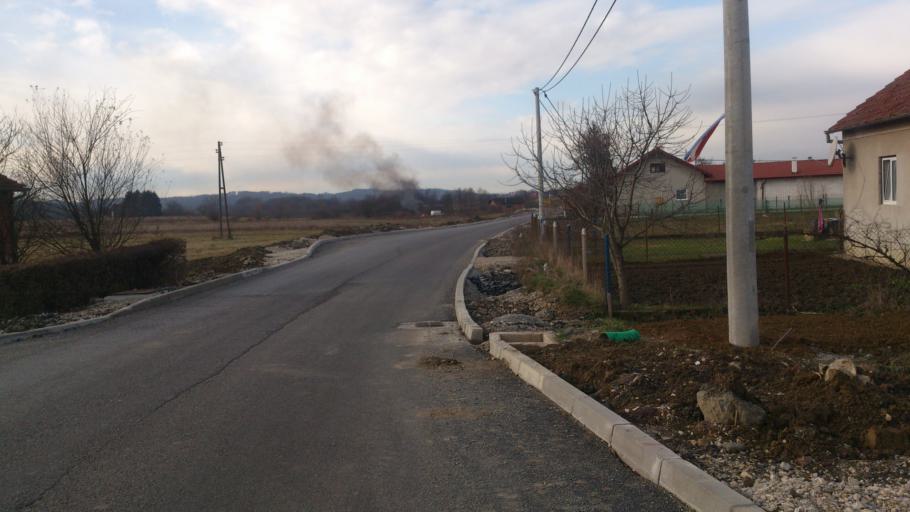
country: HR
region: Krapinsko-Zagorska
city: Marija Bistrica
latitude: 46.0503
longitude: 16.1168
